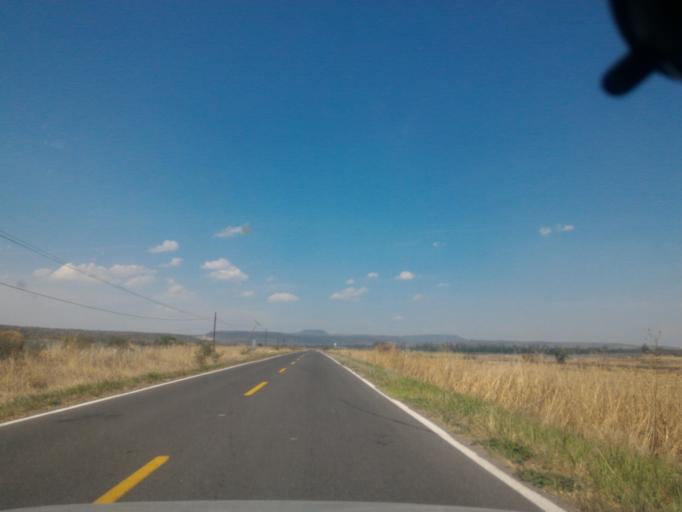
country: MX
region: Guanajuato
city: Ciudad Manuel Doblado
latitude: 20.8548
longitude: -101.9988
